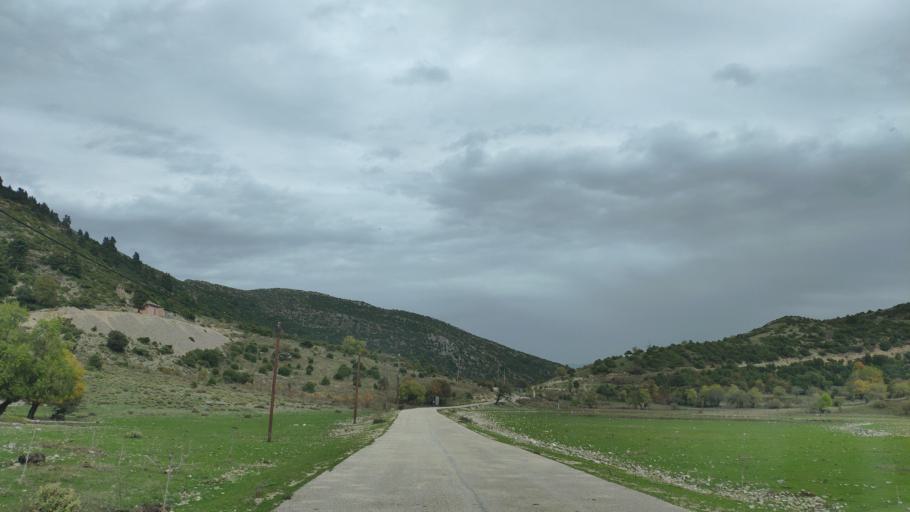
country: GR
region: Epirus
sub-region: Nomos Thesprotias
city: Paramythia
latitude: 39.4476
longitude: 20.6451
